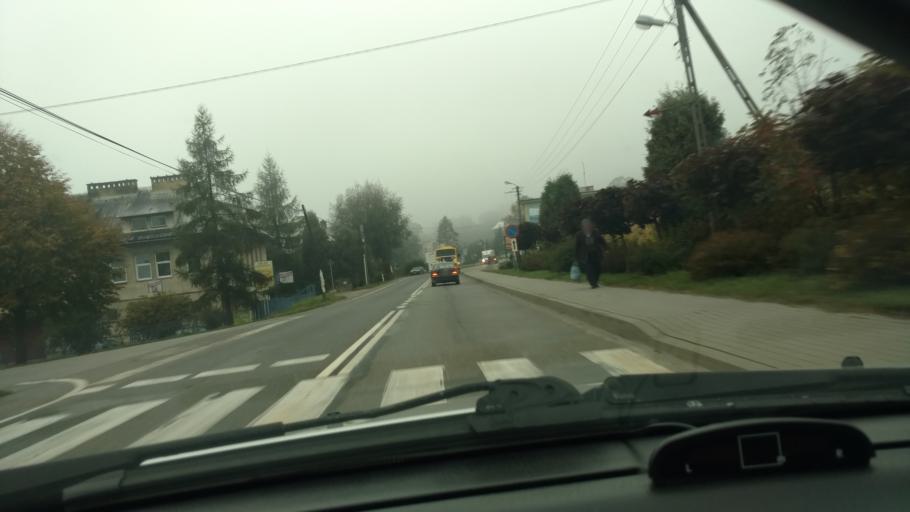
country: PL
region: Subcarpathian Voivodeship
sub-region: Powiat strzyzowski
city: Wisniowa
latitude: 49.8683
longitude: 21.6528
